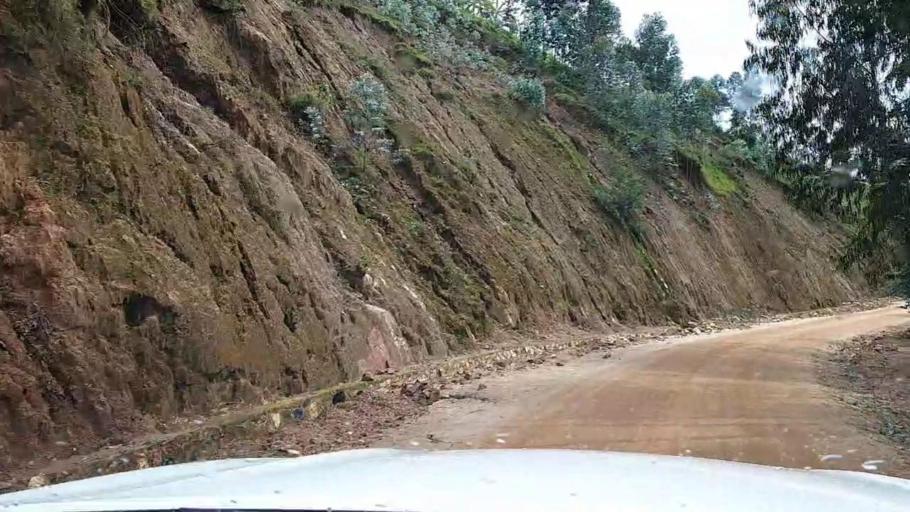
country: RW
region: Southern Province
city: Nzega
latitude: -2.4527
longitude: 29.4656
